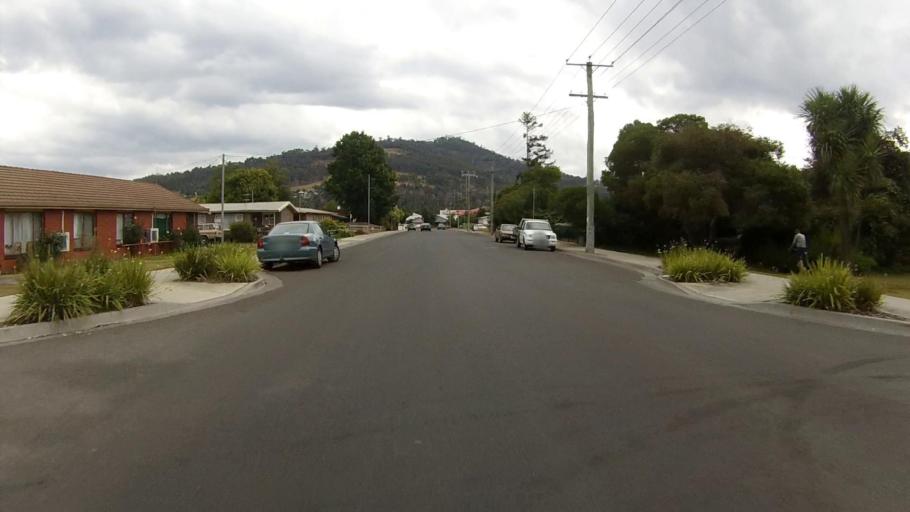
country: AU
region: Tasmania
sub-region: Huon Valley
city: Huonville
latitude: -43.0300
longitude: 147.0528
